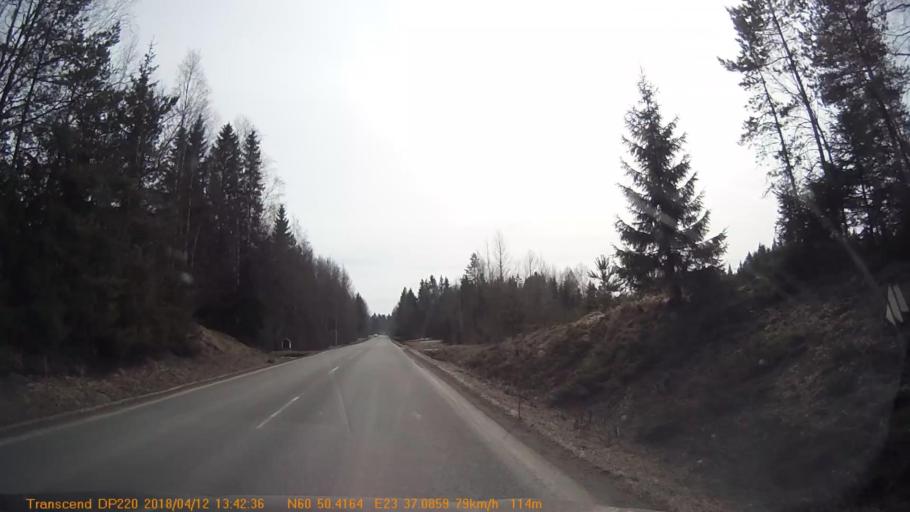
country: FI
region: Haeme
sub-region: Forssa
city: Forssa
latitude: 60.8396
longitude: 23.6181
